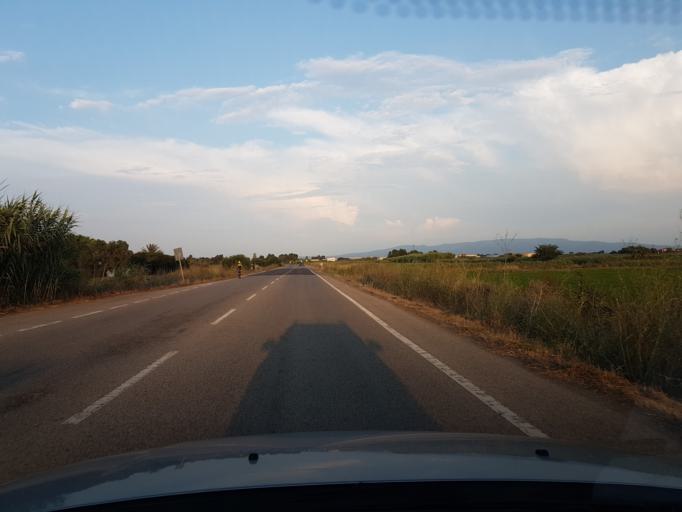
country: IT
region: Sardinia
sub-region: Provincia di Oristano
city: Cabras
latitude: 39.9187
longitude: 8.5246
